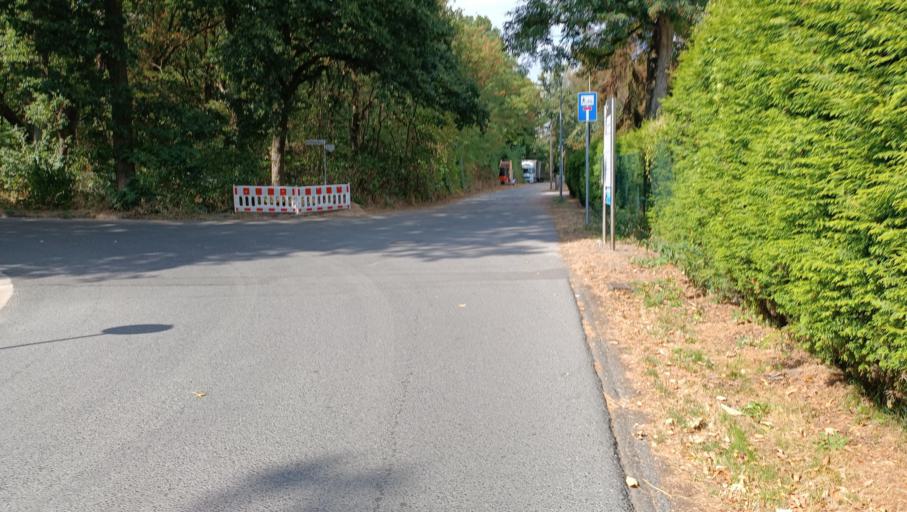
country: DE
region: North Rhine-Westphalia
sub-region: Regierungsbezirk Dusseldorf
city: Moers
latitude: 51.4318
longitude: 6.6510
